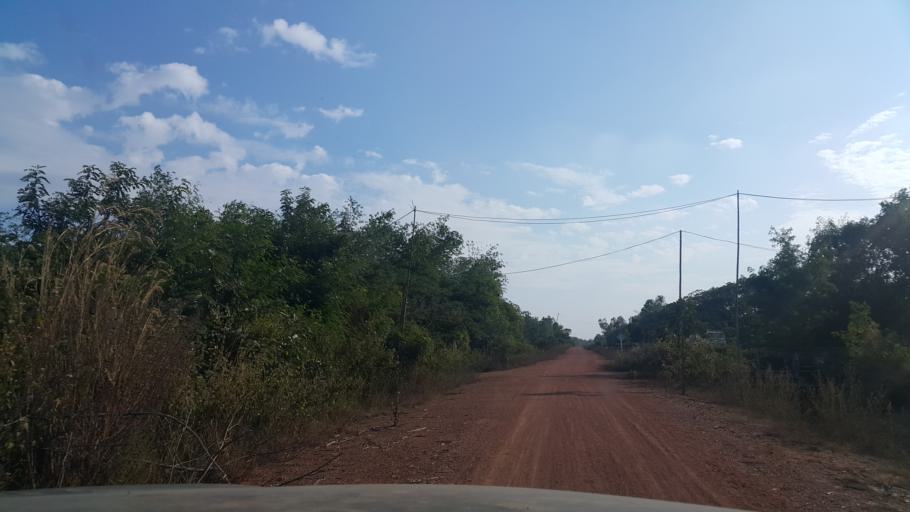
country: TH
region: Lampang
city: Hang Chat
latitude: 18.2736
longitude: 99.3721
